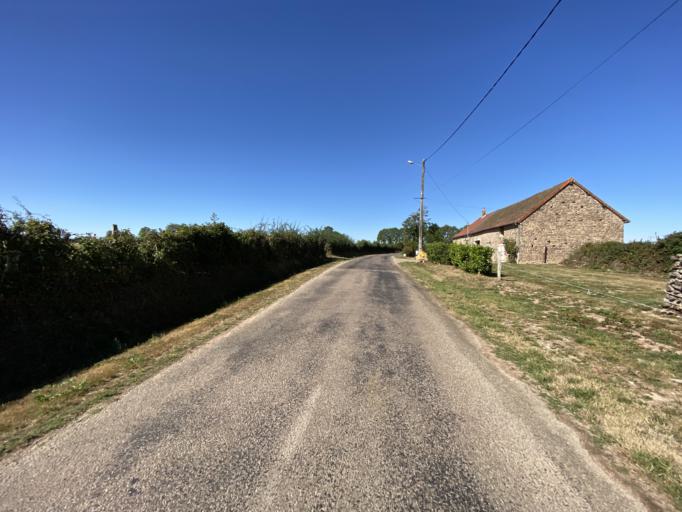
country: FR
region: Bourgogne
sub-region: Departement de la Cote-d'Or
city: Saulieu
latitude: 47.2760
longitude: 4.1936
